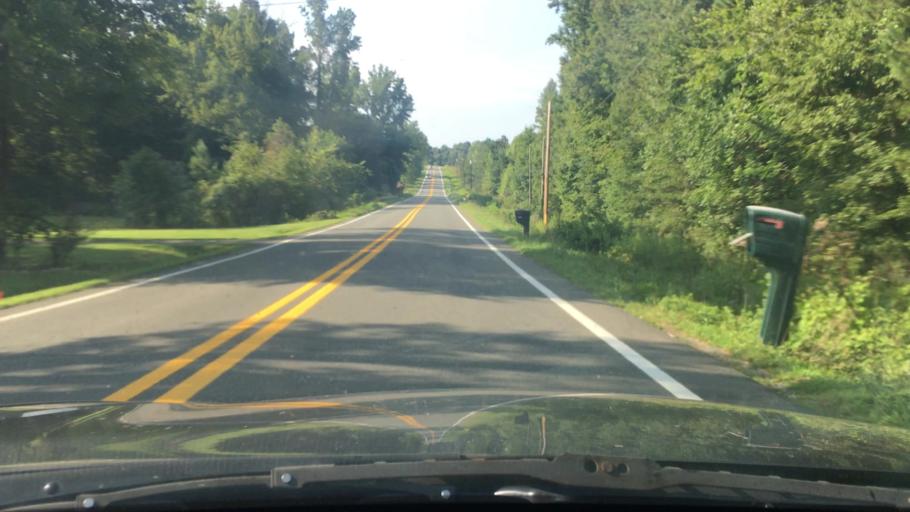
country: US
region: North Carolina
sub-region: Alamance County
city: Green Level
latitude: 36.2360
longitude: -79.3224
